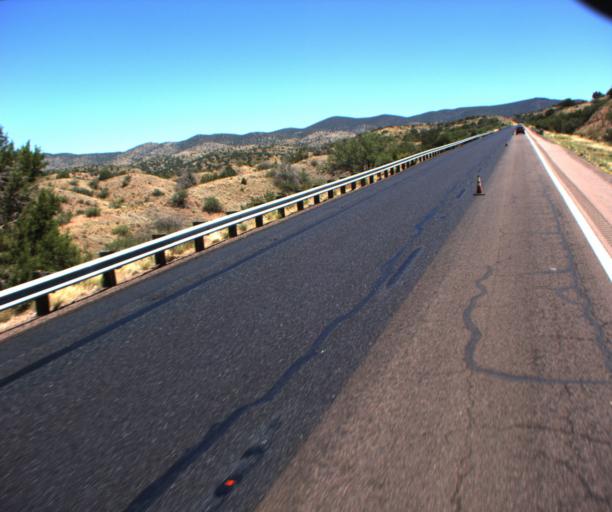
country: US
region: Arizona
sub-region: Gila County
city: Payson
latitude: 34.1164
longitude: -111.3497
